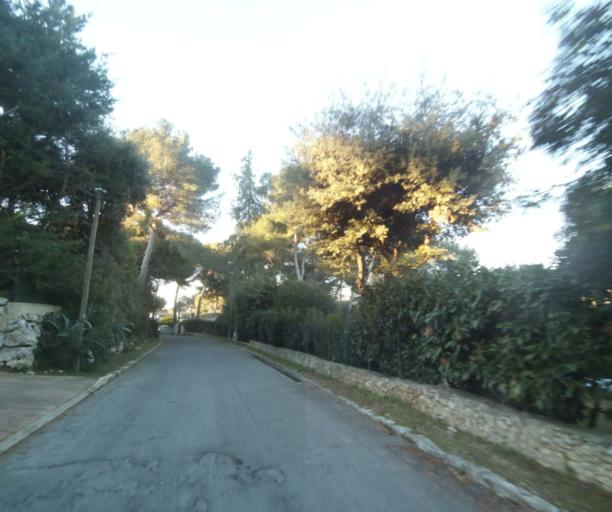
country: FR
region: Provence-Alpes-Cote d'Azur
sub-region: Departement des Alpes-Maritimes
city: Vallauris
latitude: 43.5841
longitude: 7.0825
